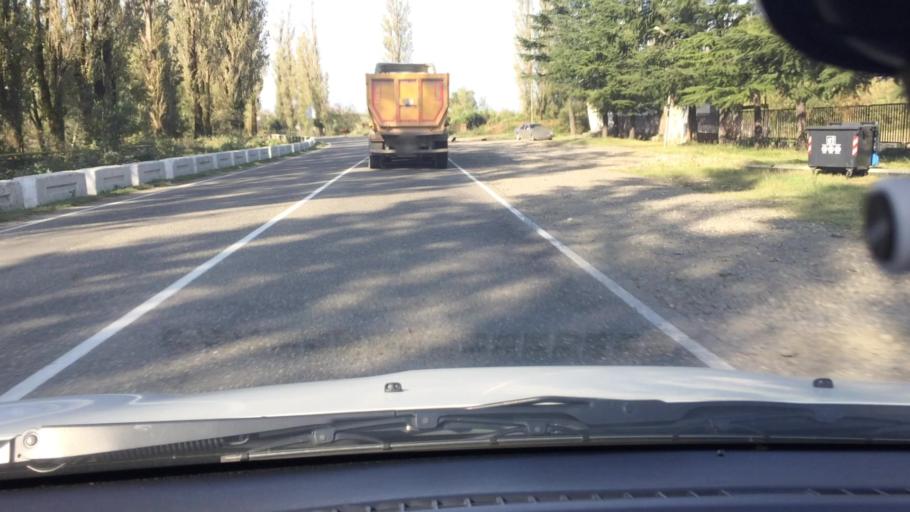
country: GE
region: Guria
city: Lanchkhuti
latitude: 42.0875
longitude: 42.0141
